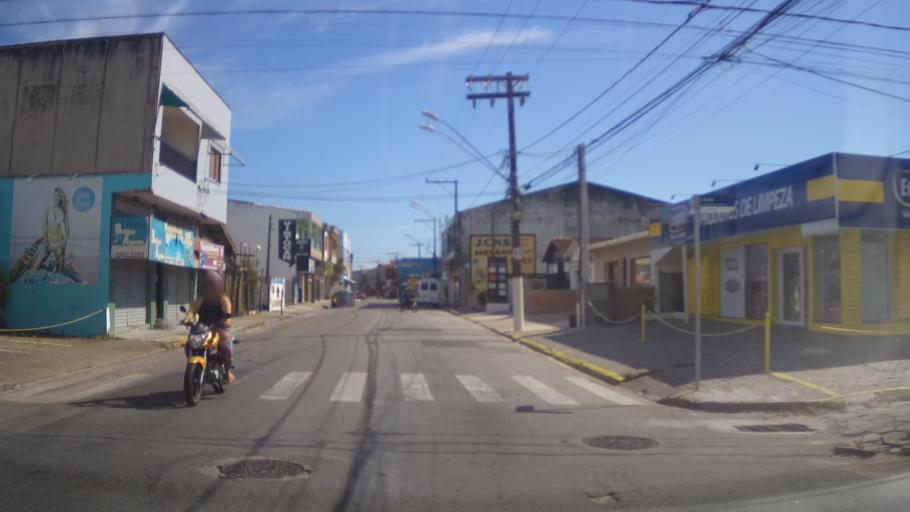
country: BR
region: Sao Paulo
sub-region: Itanhaem
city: Itanhaem
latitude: -24.1941
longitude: -46.8071
